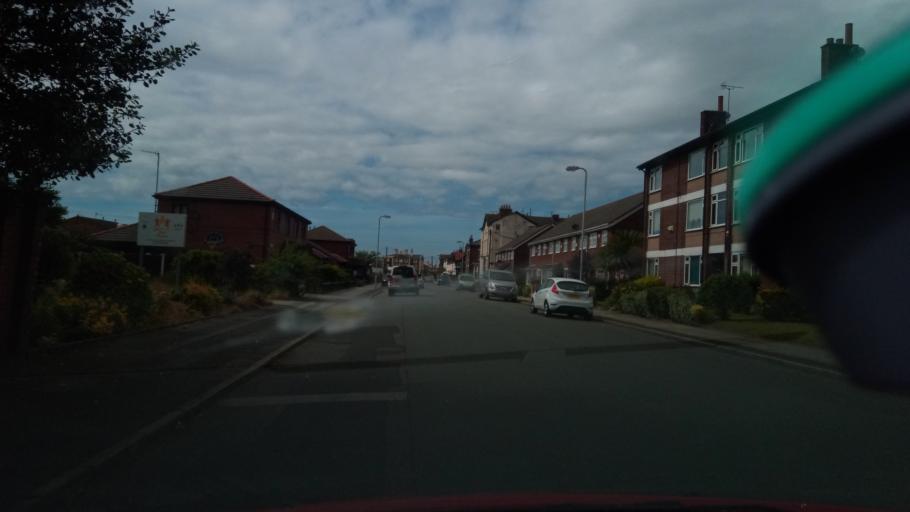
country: GB
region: England
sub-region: Sefton
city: Bootle
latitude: 53.4693
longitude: -3.0241
